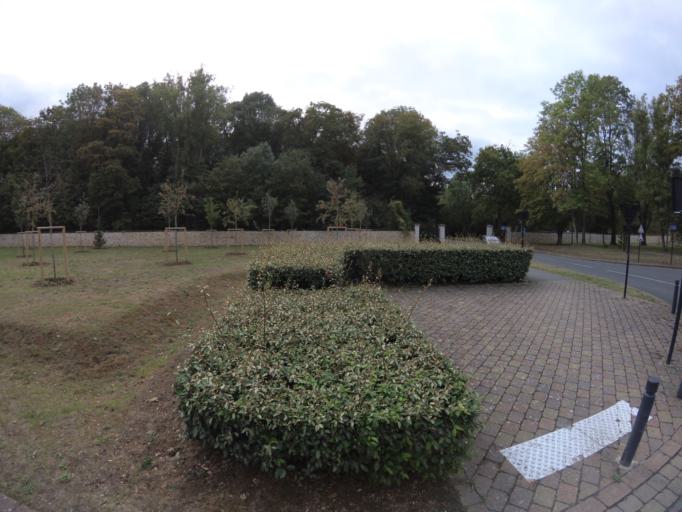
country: FR
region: Ile-de-France
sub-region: Departement de Seine-et-Marne
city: Chessy
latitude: 48.8767
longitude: 2.7707
